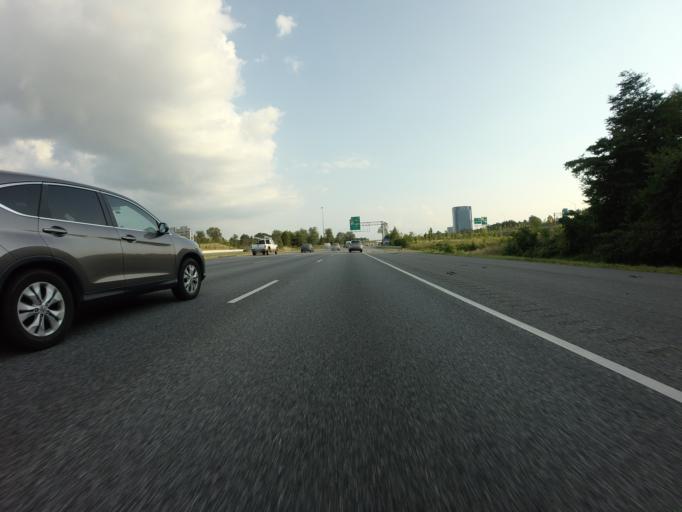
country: US
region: Maryland
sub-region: Prince George's County
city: West Laurel
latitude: 39.0932
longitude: -76.8920
